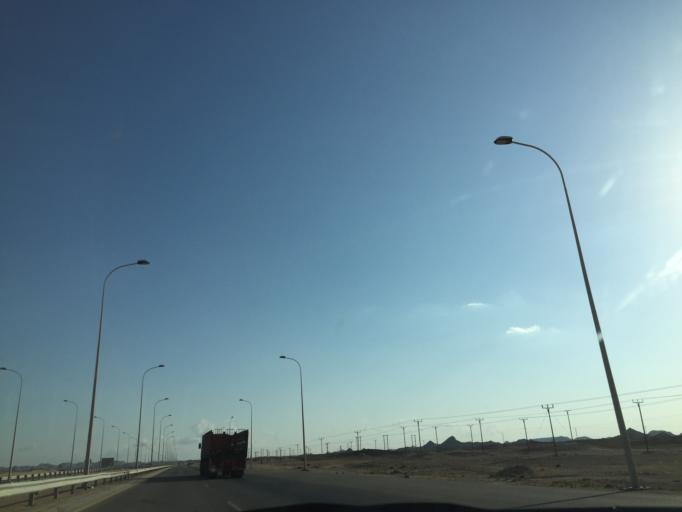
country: OM
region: Zufar
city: Salalah
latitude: 17.5301
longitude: 54.0557
